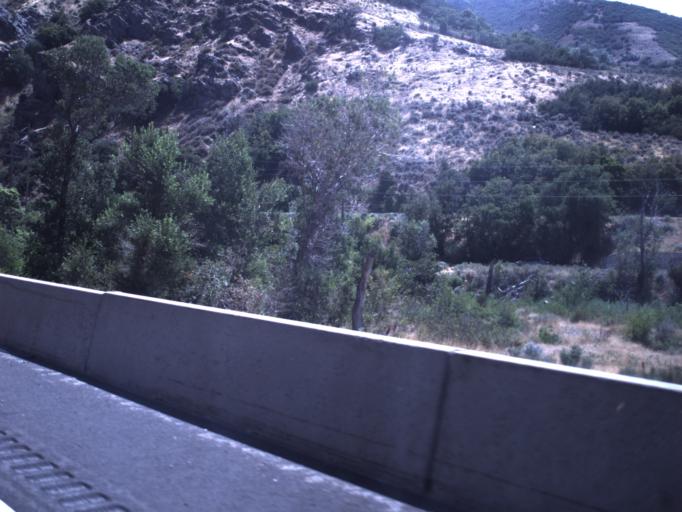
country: US
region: Utah
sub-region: Weber County
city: Uintah
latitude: 41.1362
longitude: -111.8992
